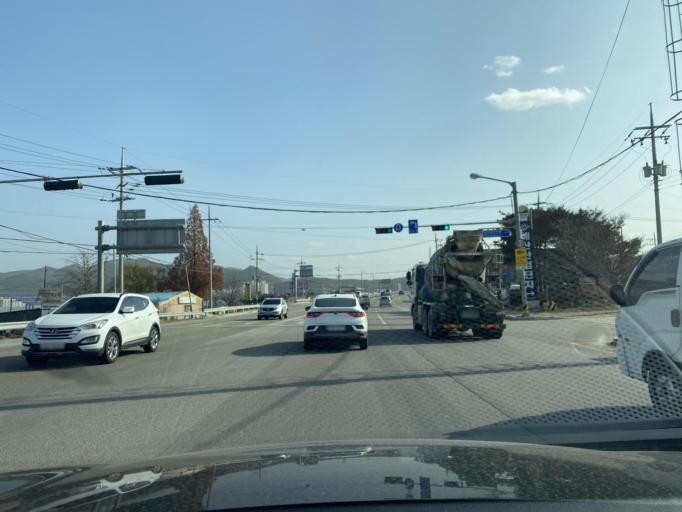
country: KR
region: Chungcheongnam-do
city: Yesan
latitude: 36.6849
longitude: 126.8158
